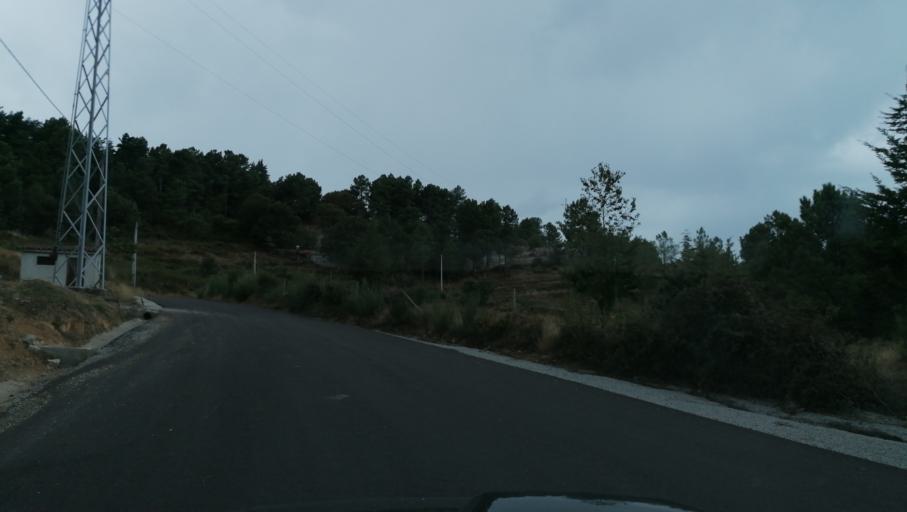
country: PT
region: Vila Real
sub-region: Vila Pouca de Aguiar
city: Vila Pouca de Aguiar
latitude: 41.5617
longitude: -7.6586
